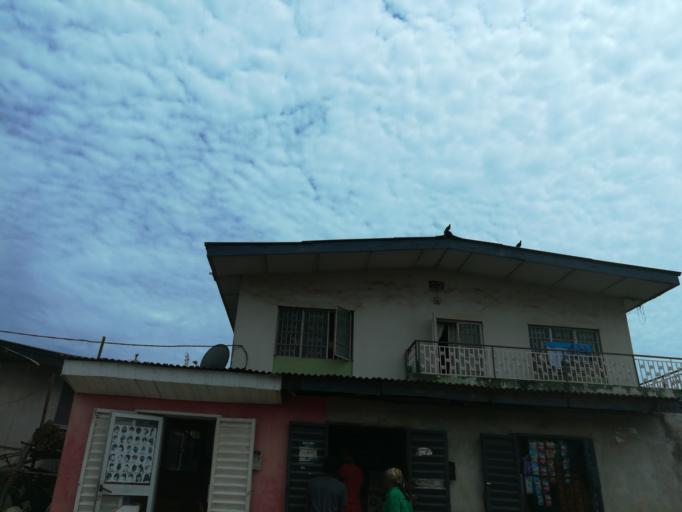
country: NG
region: Lagos
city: Oshodi
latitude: 6.5600
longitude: 3.3299
